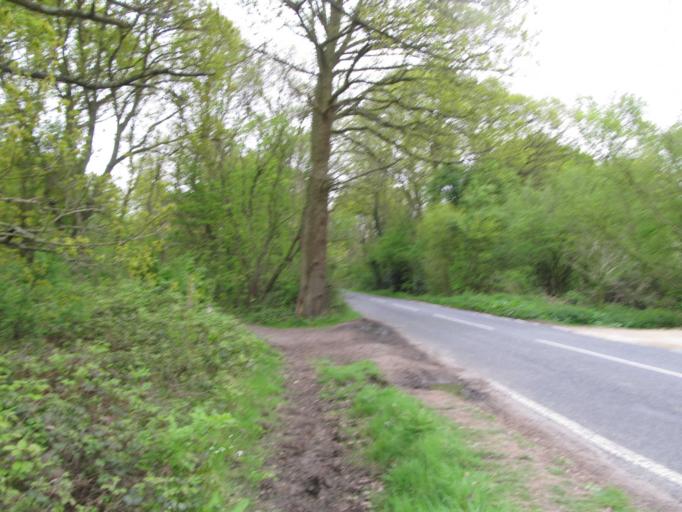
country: GB
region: England
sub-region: Royal Borough of Windsor and Maidenhead
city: Bisham
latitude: 51.5466
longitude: -0.7577
